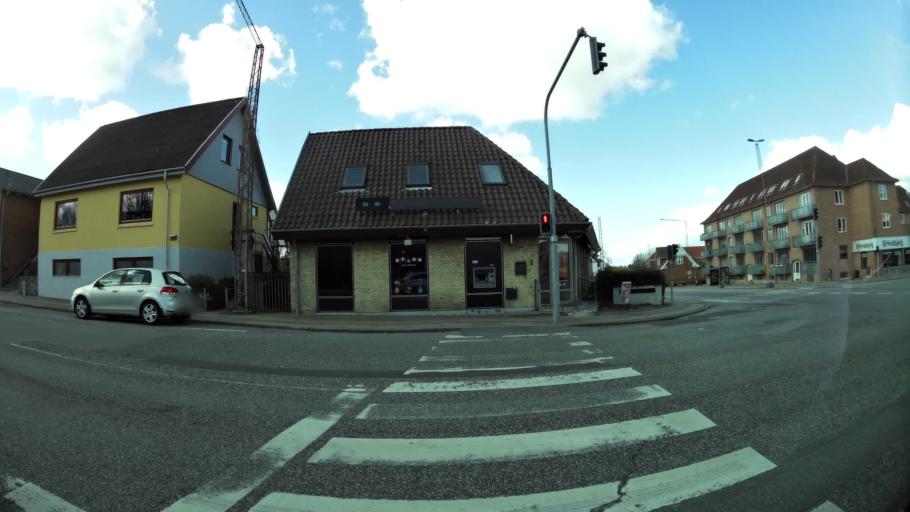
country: DK
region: North Denmark
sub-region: Alborg Kommune
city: Aalborg
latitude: 57.0698
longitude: 9.9075
